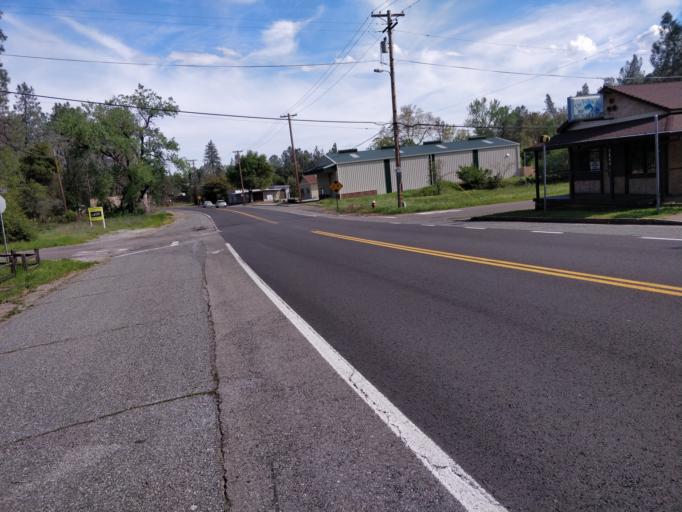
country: US
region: California
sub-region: Shasta County
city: Central Valley (historical)
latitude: 40.6835
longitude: -122.3777
